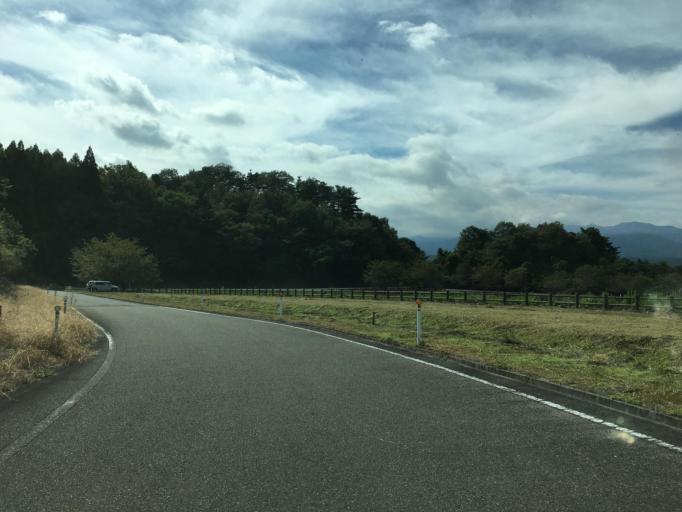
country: JP
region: Fukushima
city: Nihommatsu
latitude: 37.6296
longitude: 140.4194
